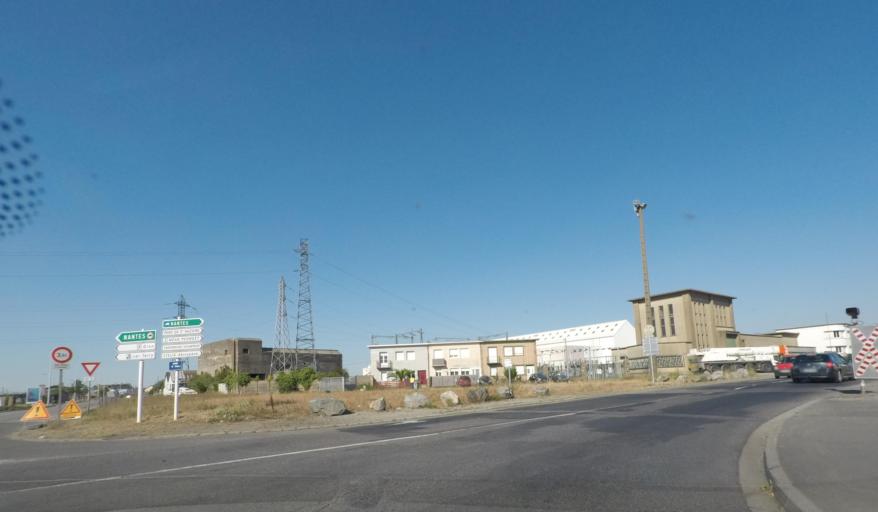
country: FR
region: Pays de la Loire
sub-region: Departement de la Loire-Atlantique
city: Saint-Nazaire
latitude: 47.2905
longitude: -2.1995
